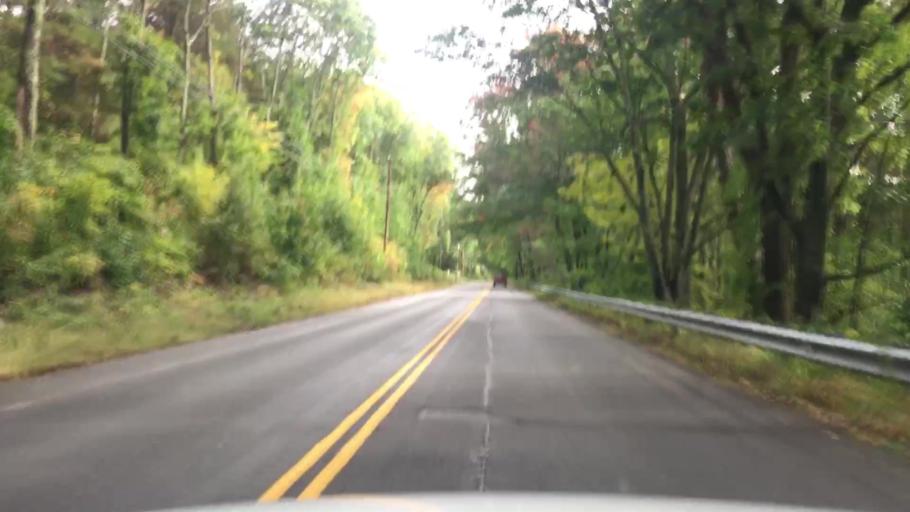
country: US
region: Maine
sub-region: Cumberland County
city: Yarmouth
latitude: 43.7727
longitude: -70.1925
